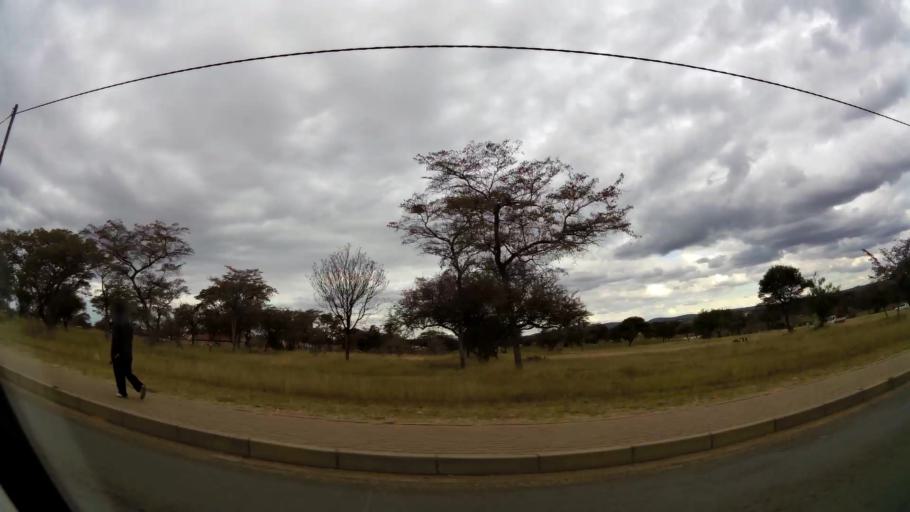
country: ZA
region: Limpopo
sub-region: Waterberg District Municipality
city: Modimolle
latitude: -24.6988
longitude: 28.4179
